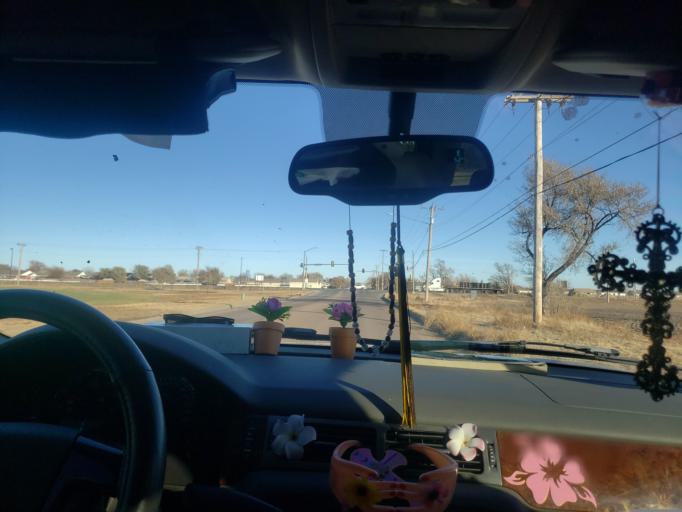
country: US
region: Kansas
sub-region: Finney County
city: Garden City
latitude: 37.9677
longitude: -100.8410
